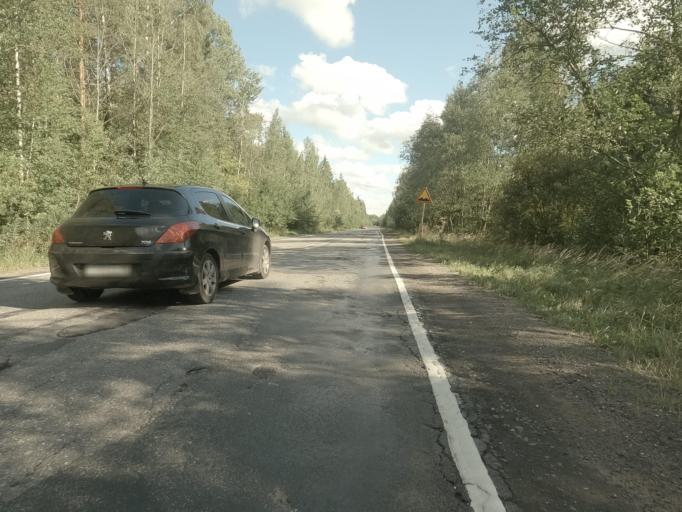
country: RU
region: Leningrad
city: Shcheglovo
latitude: 59.9923
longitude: 30.8815
